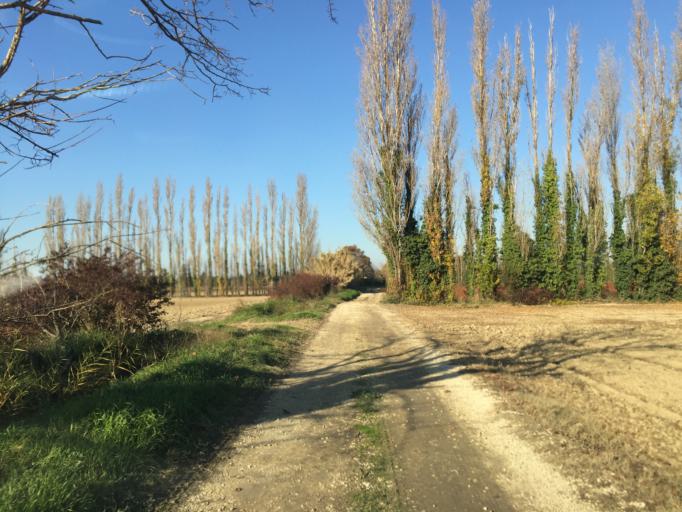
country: FR
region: Provence-Alpes-Cote d'Azur
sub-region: Departement du Vaucluse
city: Jonquieres
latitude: 44.1261
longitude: 4.9218
